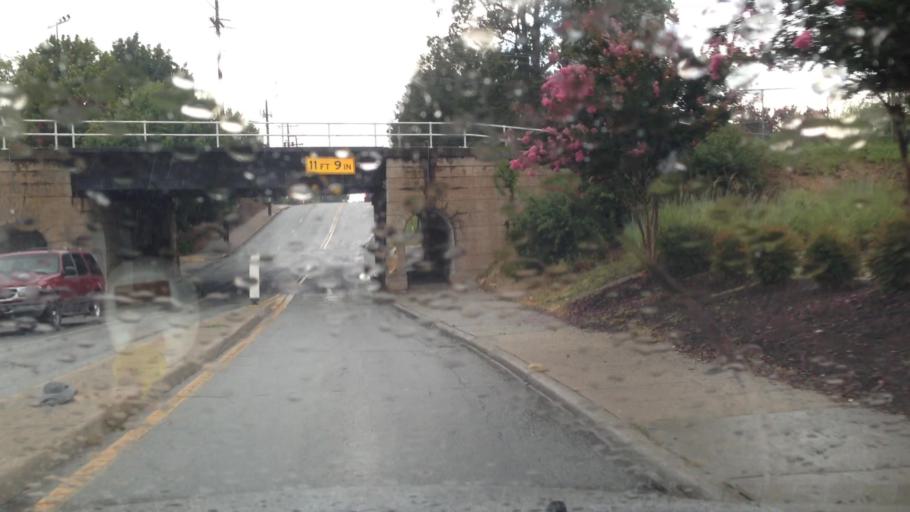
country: US
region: North Carolina
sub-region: Guilford County
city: Greensboro
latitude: 36.0627
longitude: -79.8154
